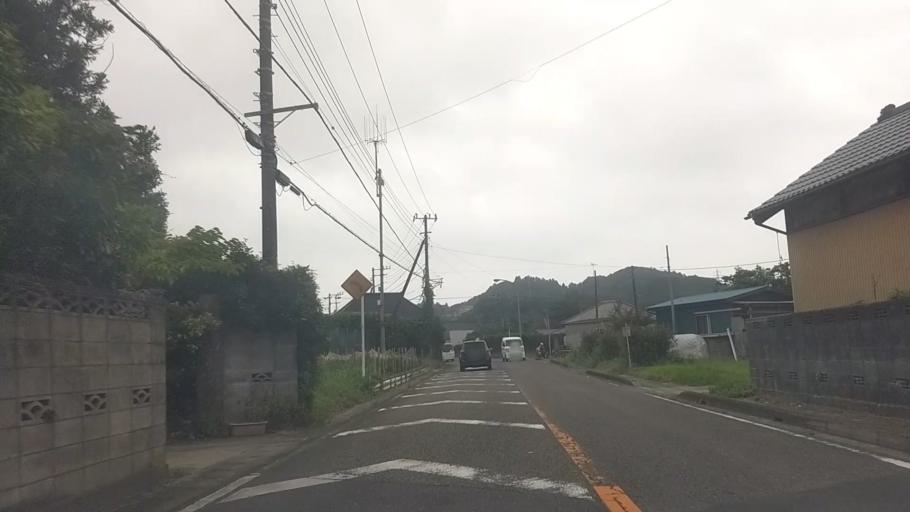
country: JP
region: Chiba
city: Ohara
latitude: 35.2610
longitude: 140.3769
